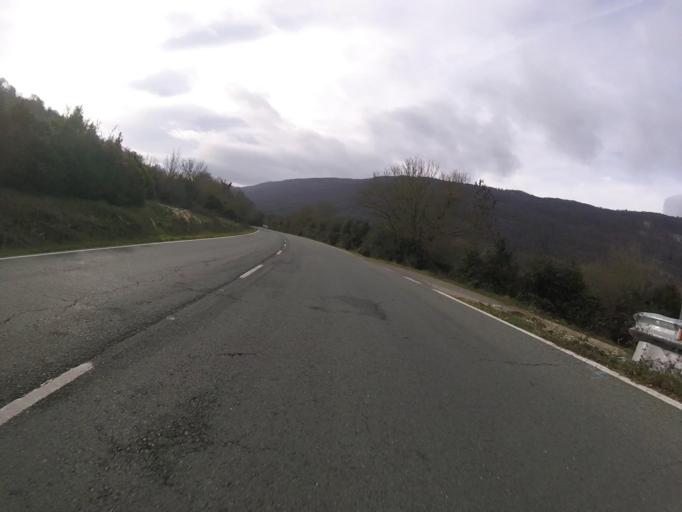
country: ES
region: Navarre
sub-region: Provincia de Navarra
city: Lezaun
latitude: 42.8362
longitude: -2.0268
